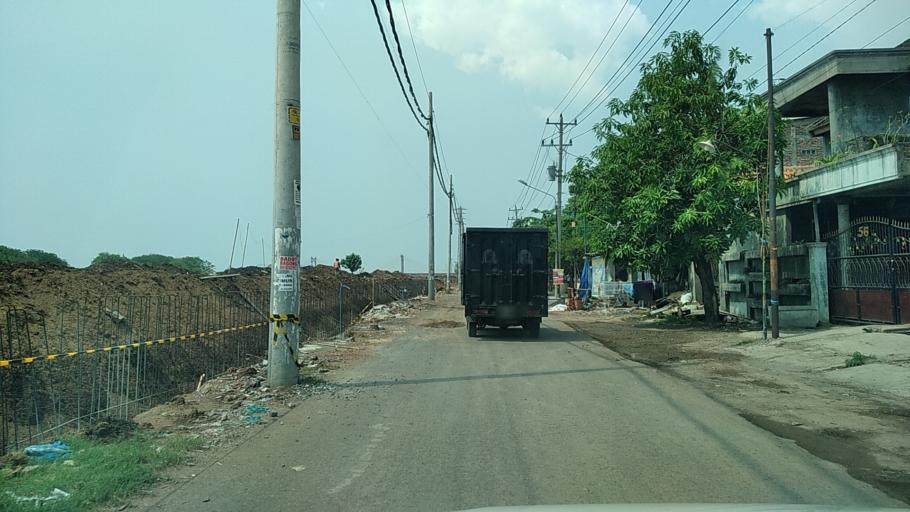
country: ID
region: Central Java
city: Semarang
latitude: -6.9904
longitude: 110.4408
